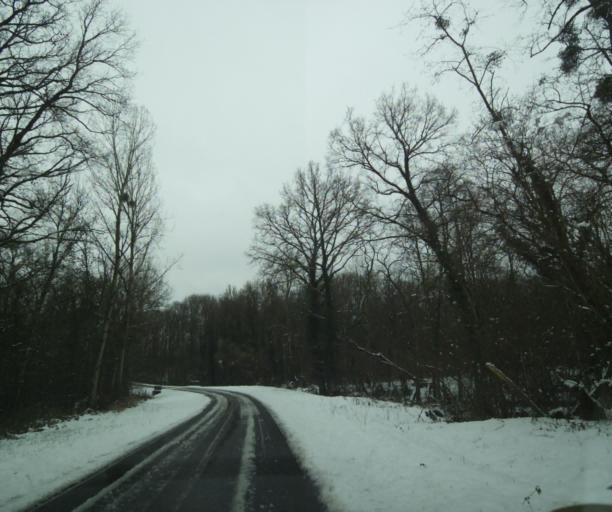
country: FR
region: Champagne-Ardenne
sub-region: Departement de la Haute-Marne
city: Montier-en-Der
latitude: 48.4262
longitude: 4.7277
